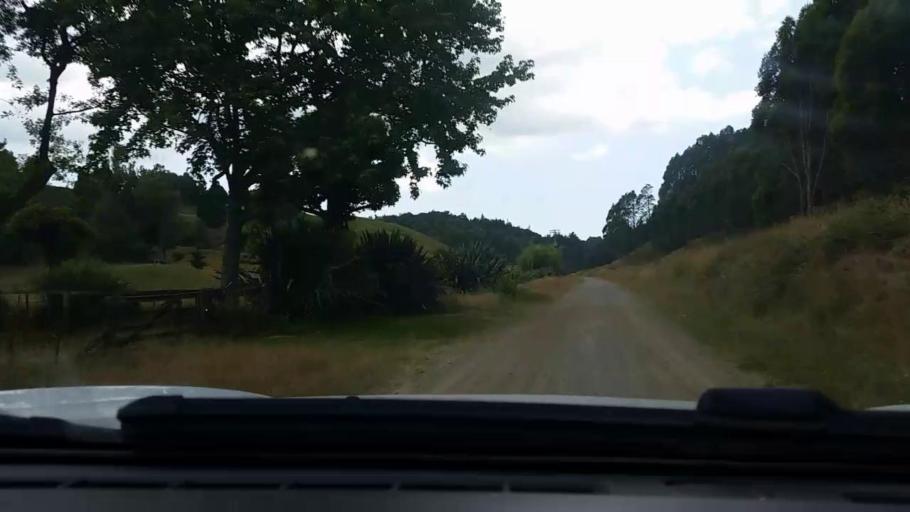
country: NZ
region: Bay of Plenty
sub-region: Kawerau District
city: Kawerau
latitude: -38.0152
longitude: 176.5971
